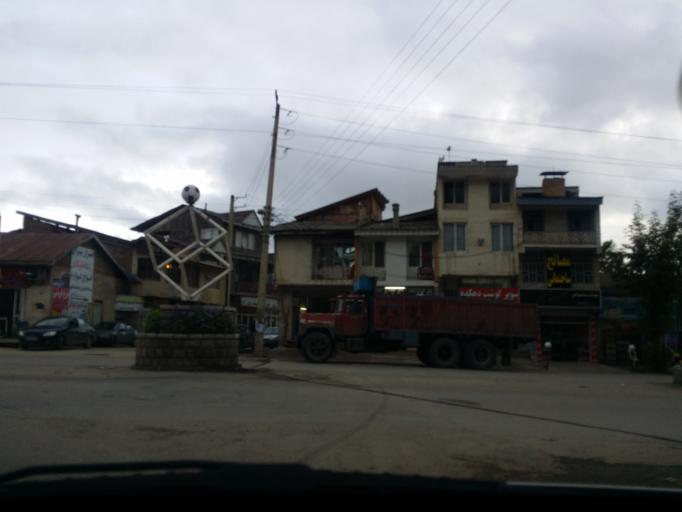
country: IR
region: Mazandaran
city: `Abbasabad
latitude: 36.5079
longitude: 51.1853
